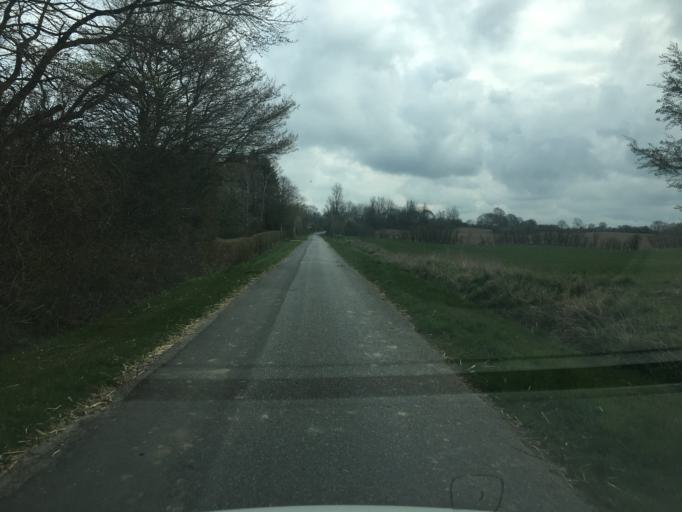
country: DE
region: Schleswig-Holstein
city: Glucksburg
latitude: 54.8992
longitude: 9.5055
